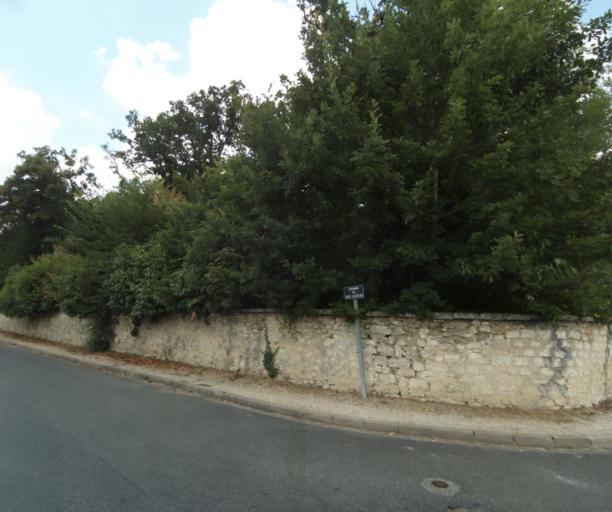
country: FR
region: Ile-de-France
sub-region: Departement de Seine-et-Marne
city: Vulaines-sur-Seine
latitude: 48.4250
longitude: 2.7687
